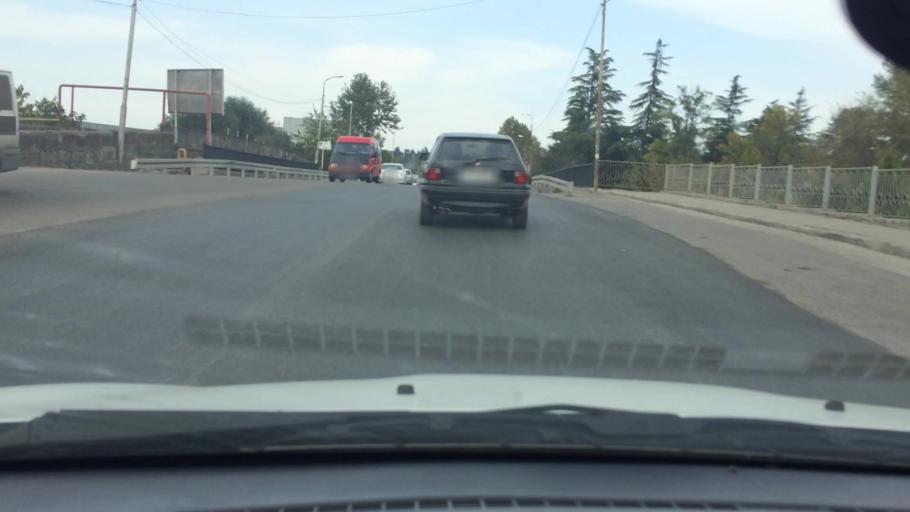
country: GE
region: Kvemo Kartli
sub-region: Marneuli
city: Marneuli
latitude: 41.4883
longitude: 44.7990
